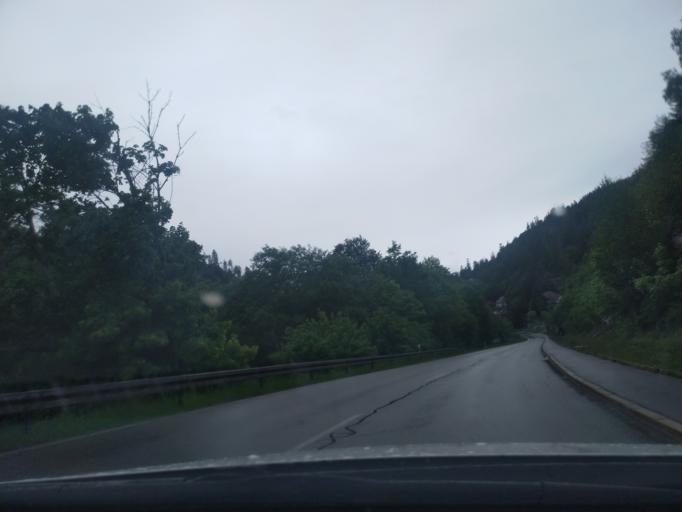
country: DE
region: Baden-Wuerttemberg
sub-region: Freiburg Region
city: Sankt Blasien
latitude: 47.7573
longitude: 8.1464
